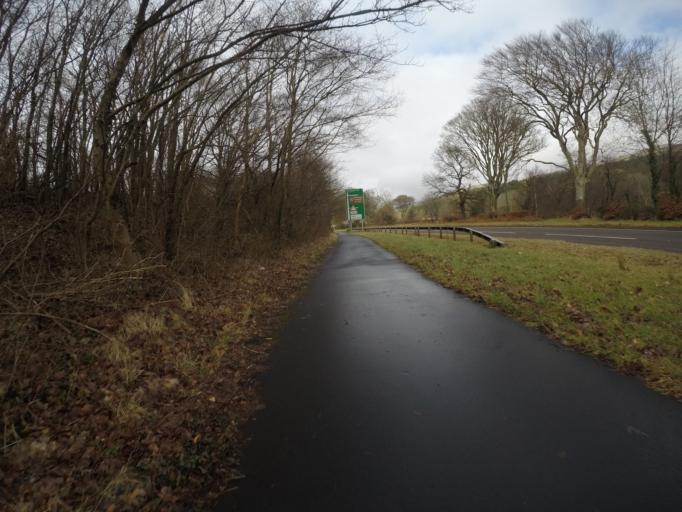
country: GB
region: Scotland
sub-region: North Ayrshire
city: Fairlie
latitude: 55.7353
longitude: -4.8617
